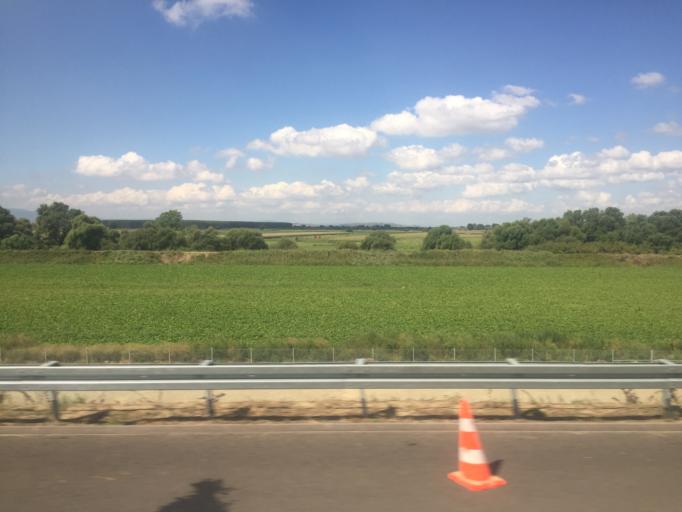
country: TR
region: Bursa
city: Tatkavakli
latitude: 40.1019
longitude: 28.2783
